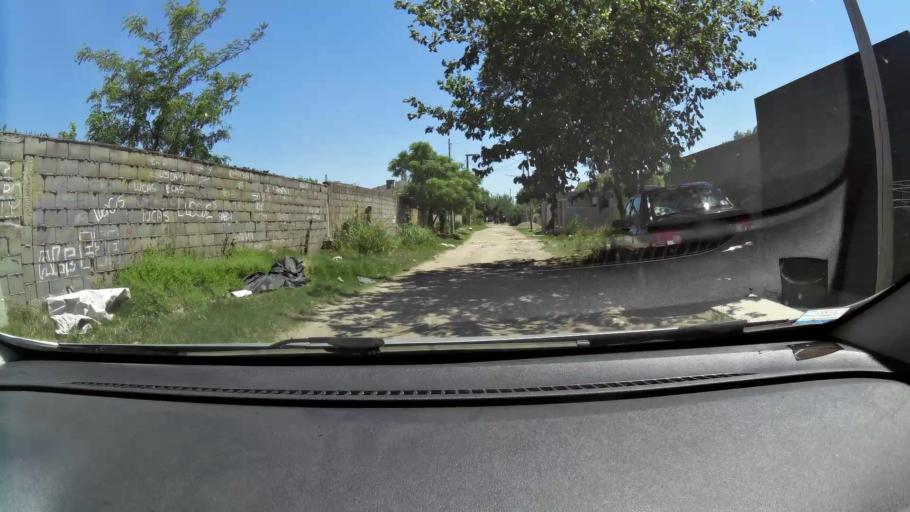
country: AR
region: Cordoba
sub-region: Departamento de Capital
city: Cordoba
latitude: -31.4389
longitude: -64.1222
